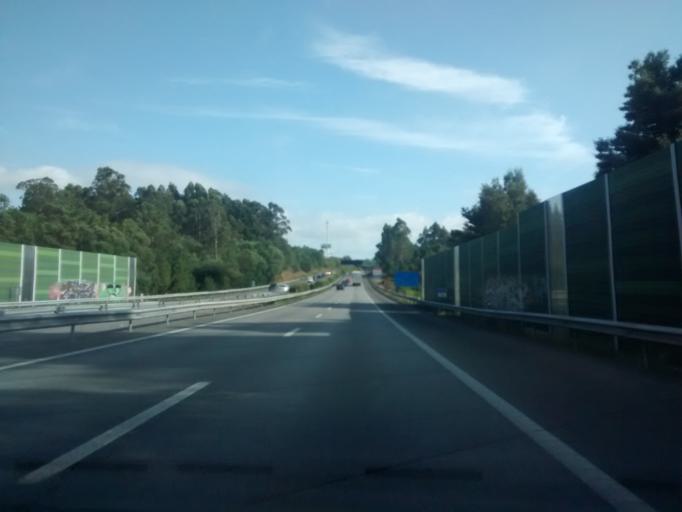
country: PT
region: Porto
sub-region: Santo Tirso
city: Santo Tirso
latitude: 41.3684
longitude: -8.5027
